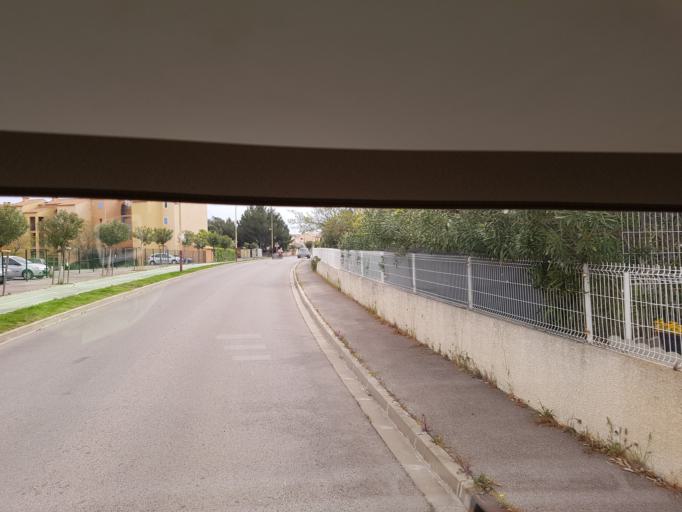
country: FR
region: Languedoc-Roussillon
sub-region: Departement de l'Aude
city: Fleury
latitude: 43.1870
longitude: 3.1904
